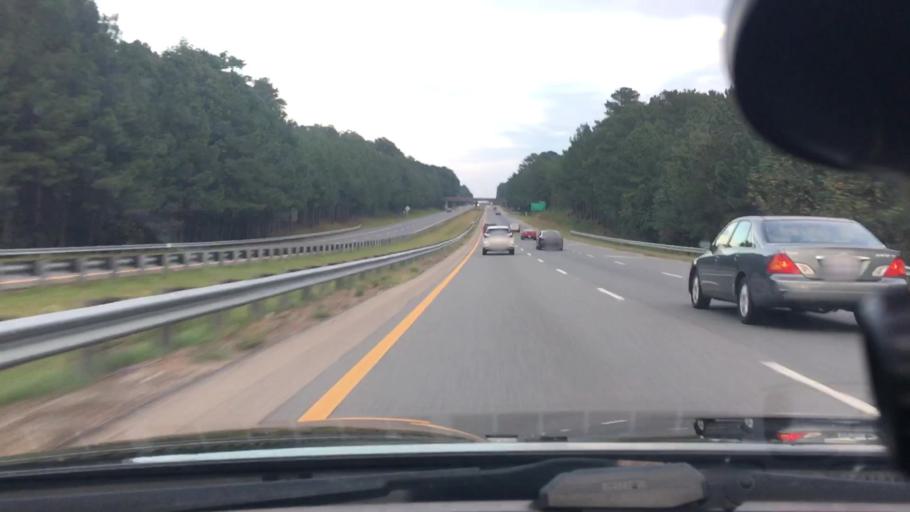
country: US
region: North Carolina
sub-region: Chatham County
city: Pittsboro
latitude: 35.6263
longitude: -79.0831
